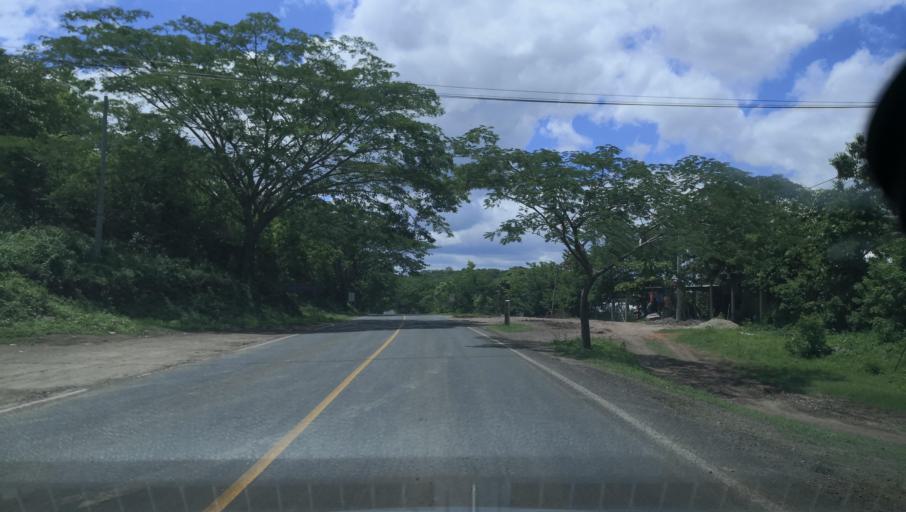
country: NI
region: Esteli
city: Condega
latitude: 13.3800
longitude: -86.4016
